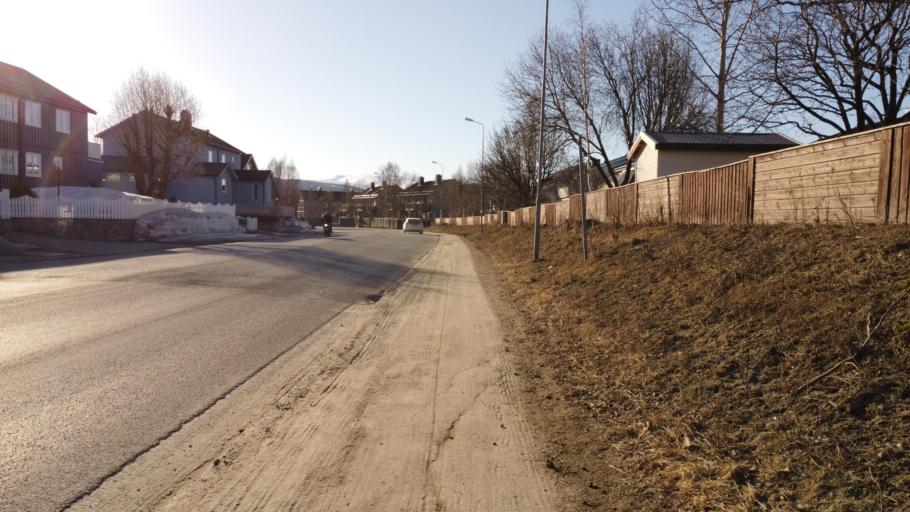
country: NO
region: Nordland
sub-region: Rana
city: Mo i Rana
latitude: 66.3193
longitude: 14.1892
